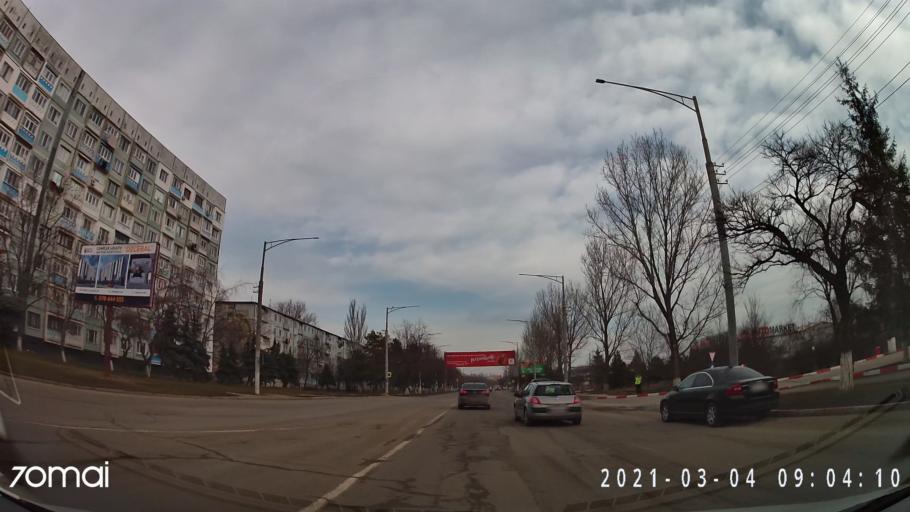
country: MD
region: Balti
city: Balti
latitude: 47.7562
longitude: 27.9414
